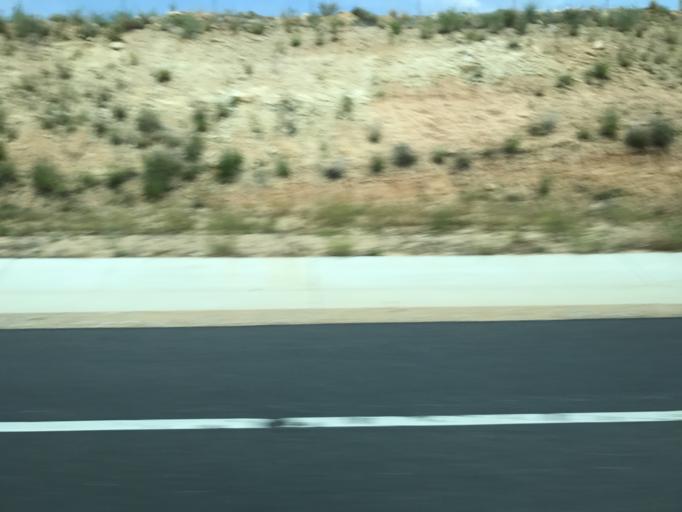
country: ES
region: Castille and Leon
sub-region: Provincia de Burgos
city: Fuentespina
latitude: 41.6417
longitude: -3.7084
